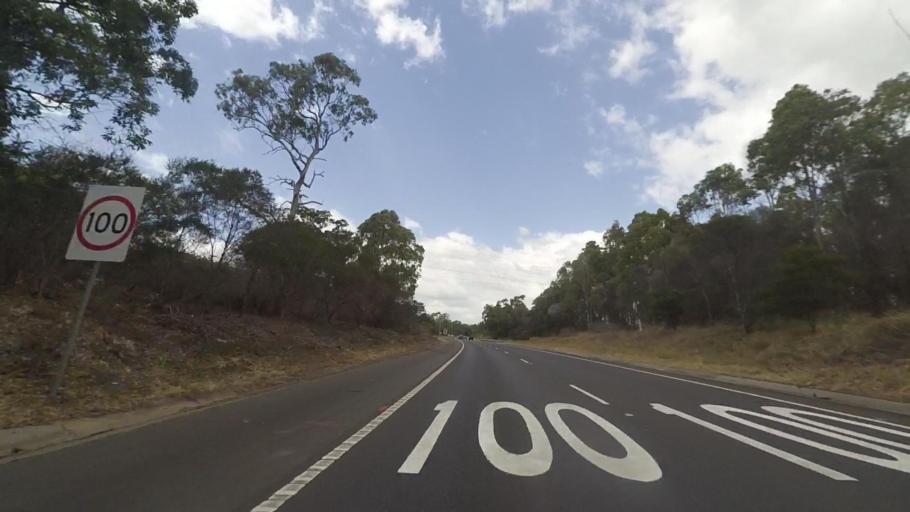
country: AU
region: New South Wales
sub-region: Wollongong
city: Dapto
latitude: -34.5290
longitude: 150.7871
